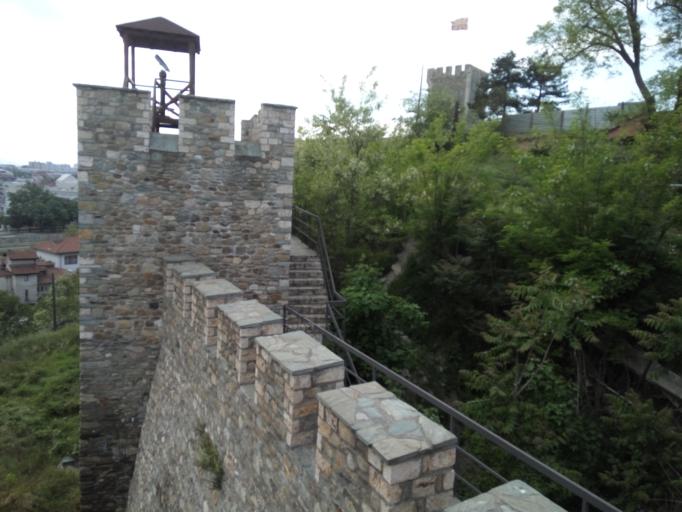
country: MK
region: Karpos
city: Skopje
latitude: 41.9999
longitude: 21.4330
